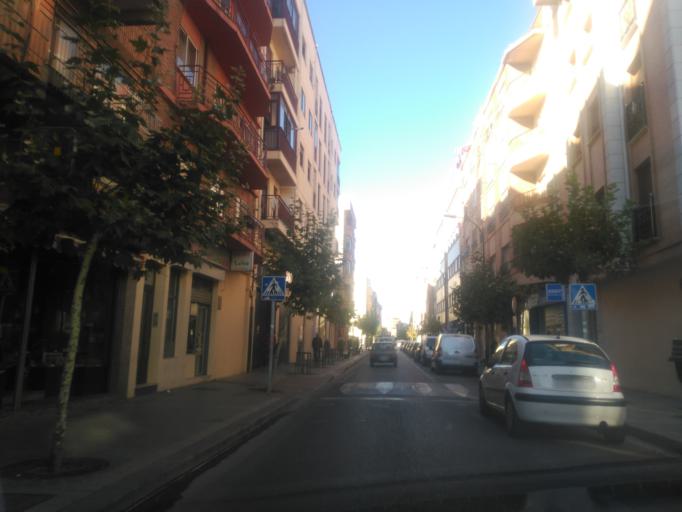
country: ES
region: Castille and Leon
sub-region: Provincia de Burgos
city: Aranda de Duero
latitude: 41.6721
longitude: -3.6818
